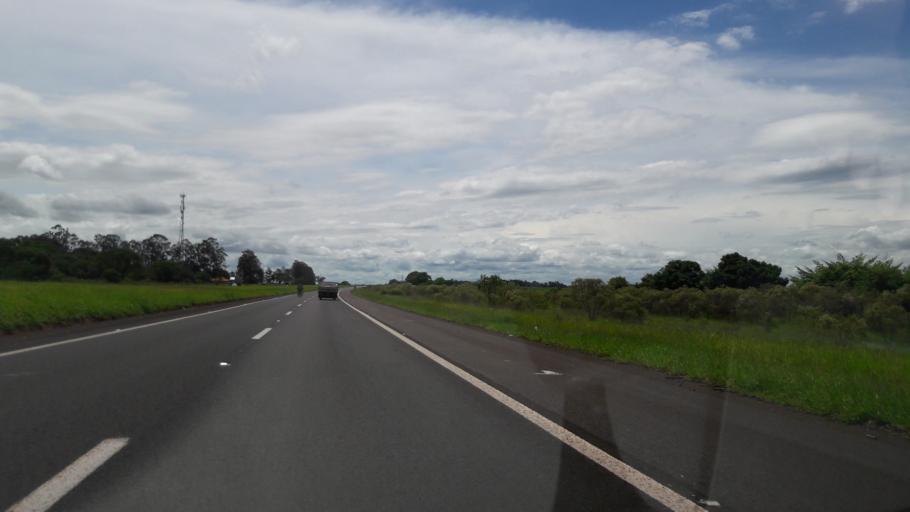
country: BR
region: Sao Paulo
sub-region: Avare
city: Avare
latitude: -22.9405
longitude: -48.9536
